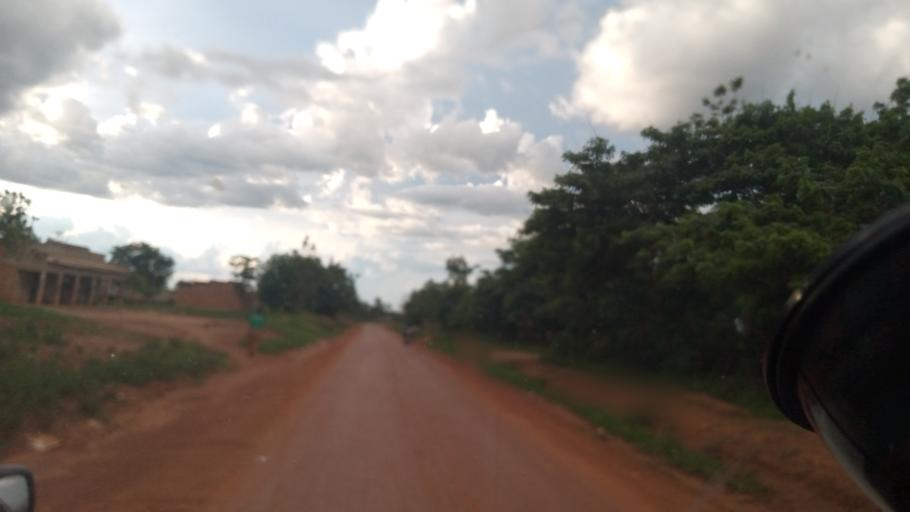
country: UG
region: Northern Region
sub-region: Lira District
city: Lira
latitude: 2.3750
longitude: 32.9342
